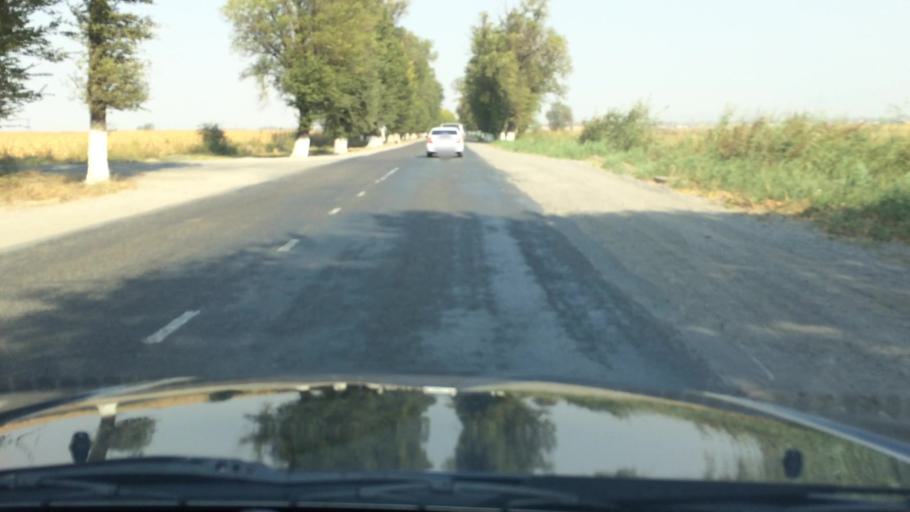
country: KG
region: Chuy
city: Lebedinovka
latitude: 42.9012
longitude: 74.6853
